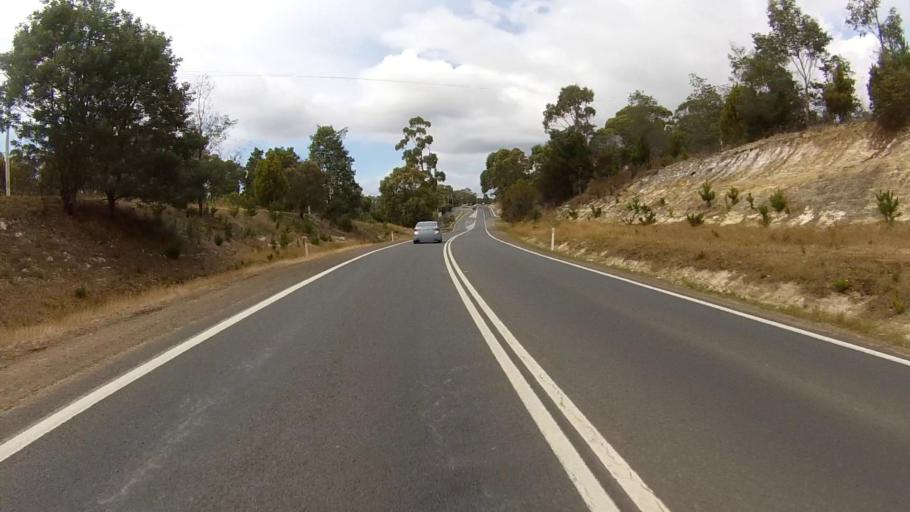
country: AU
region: Tasmania
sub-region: Kingborough
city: Margate
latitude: -43.0416
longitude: 147.2669
